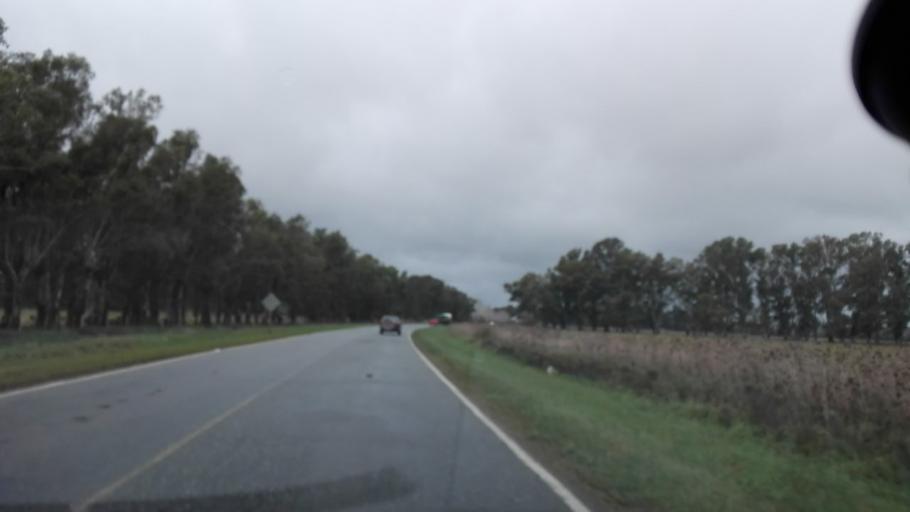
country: AR
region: Buenos Aires
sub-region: Partido de Brandsen
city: Brandsen
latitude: -35.1780
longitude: -58.3016
